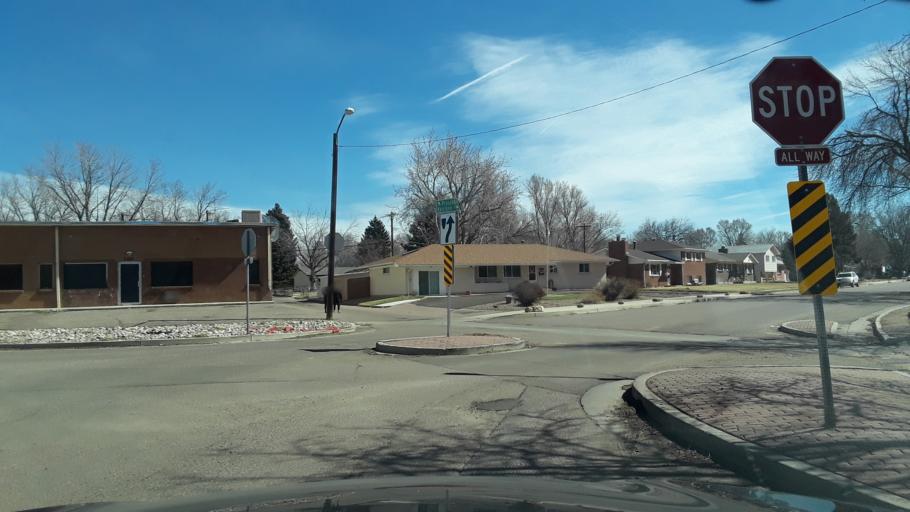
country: US
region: Colorado
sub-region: El Paso County
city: Colorado Springs
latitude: 38.8696
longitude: -104.8114
